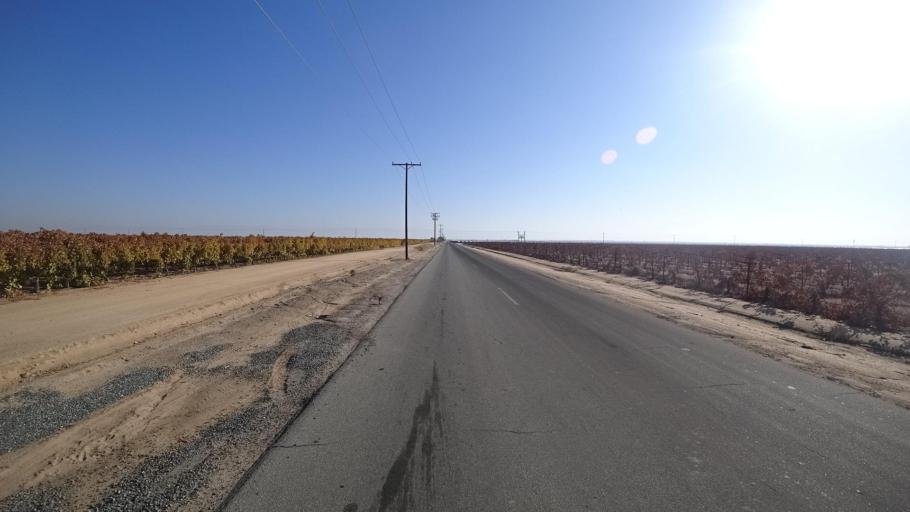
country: US
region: California
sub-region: Kern County
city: Delano
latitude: 35.7479
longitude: -119.1726
